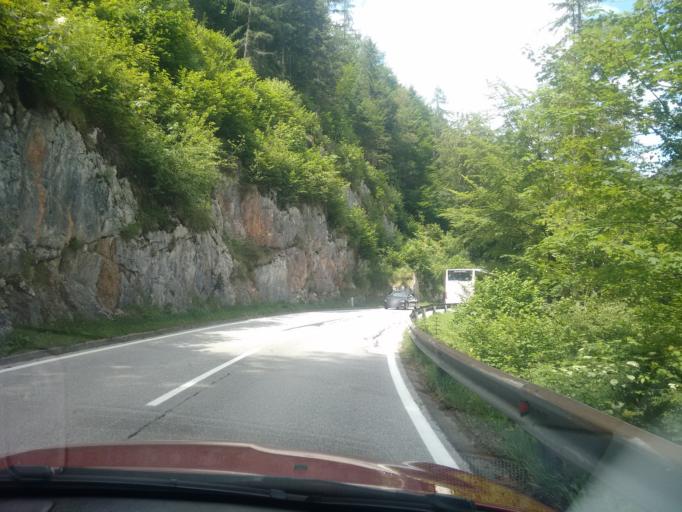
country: AT
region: Upper Austria
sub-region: Politischer Bezirk Gmunden
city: Bad Goisern
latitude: 47.5827
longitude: 13.6565
